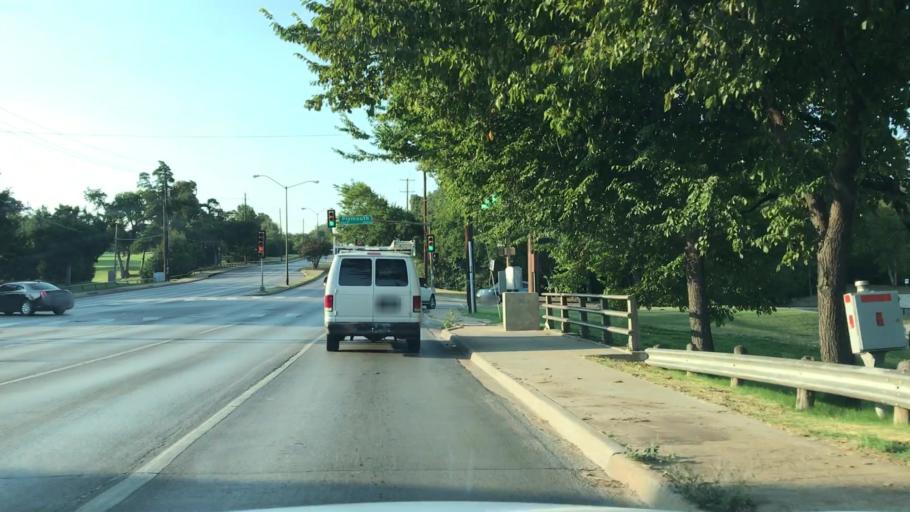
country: US
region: Texas
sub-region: Dallas County
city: Cockrell Hill
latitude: 32.7553
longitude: -96.8566
